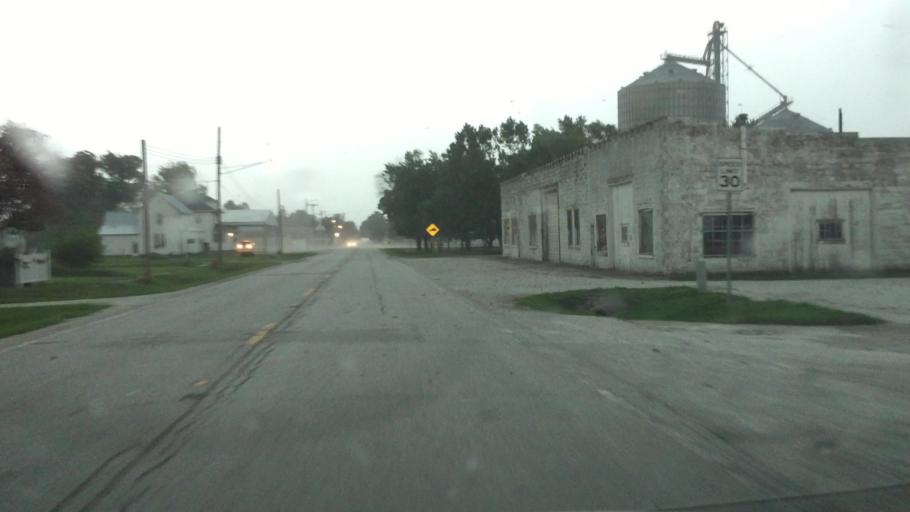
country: US
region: Illinois
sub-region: Adams County
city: Camp Point
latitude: 40.2315
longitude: -91.0597
